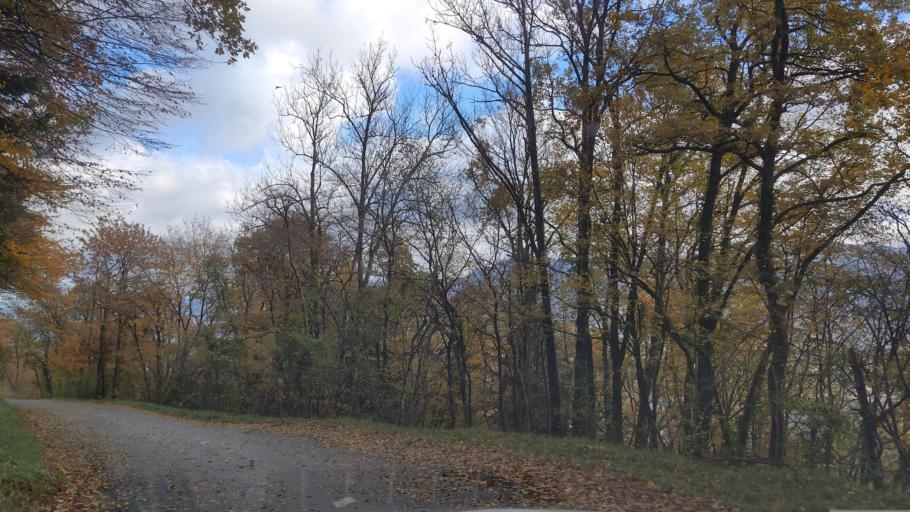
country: FR
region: Rhone-Alpes
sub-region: Departement de la Savoie
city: Le Bourget-du-Lac
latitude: 45.6517
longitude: 5.8384
